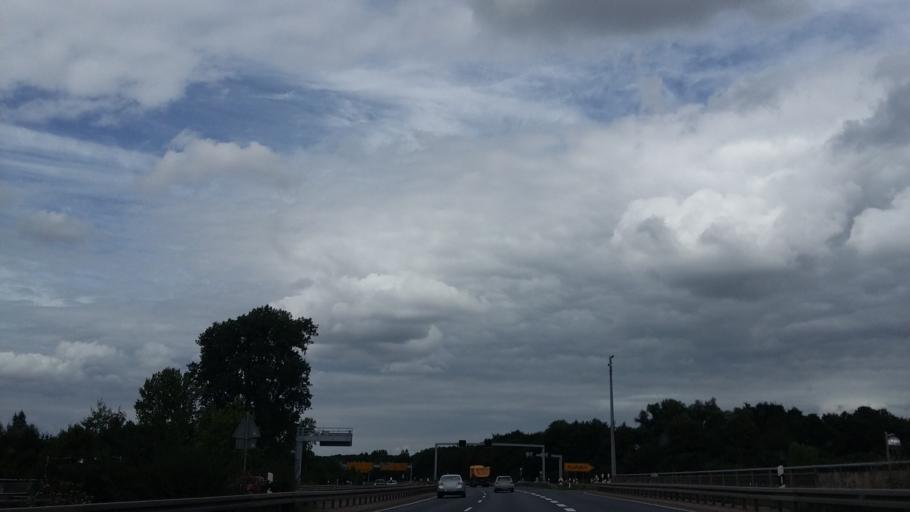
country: DE
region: Lower Saxony
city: Laatzen
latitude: 52.3316
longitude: 9.8121
